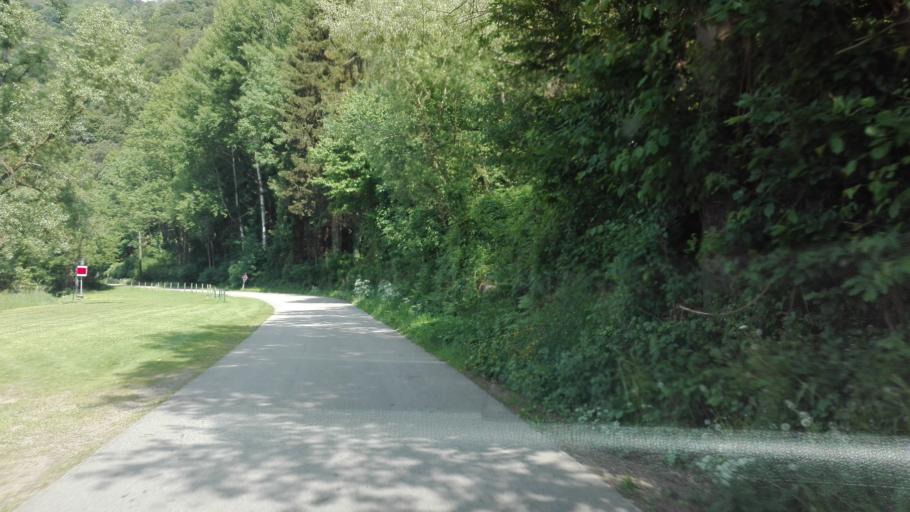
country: AT
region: Upper Austria
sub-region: Politischer Bezirk Rohrbach
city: Atzesberg
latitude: 48.4255
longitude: 13.8743
